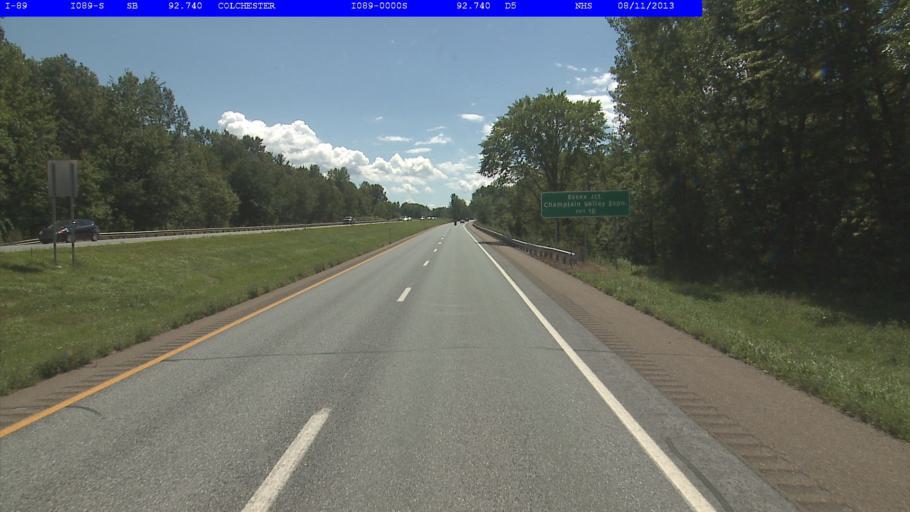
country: US
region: Vermont
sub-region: Chittenden County
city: Winooski
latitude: 44.5206
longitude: -73.1928
